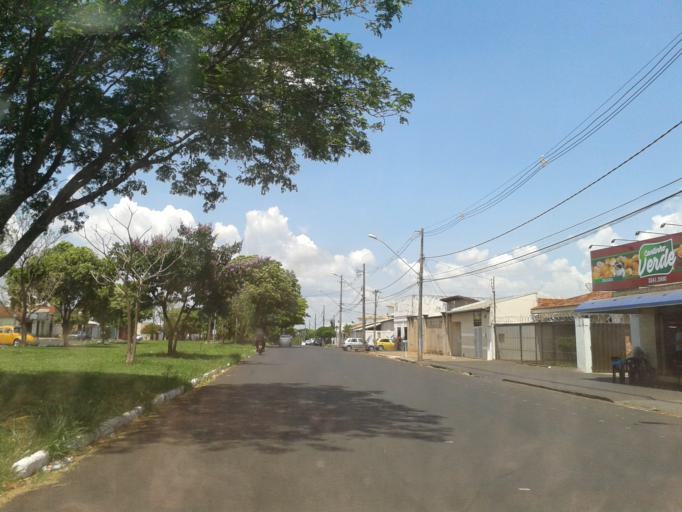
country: BR
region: Minas Gerais
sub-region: Araguari
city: Araguari
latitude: -18.6643
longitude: -48.1963
